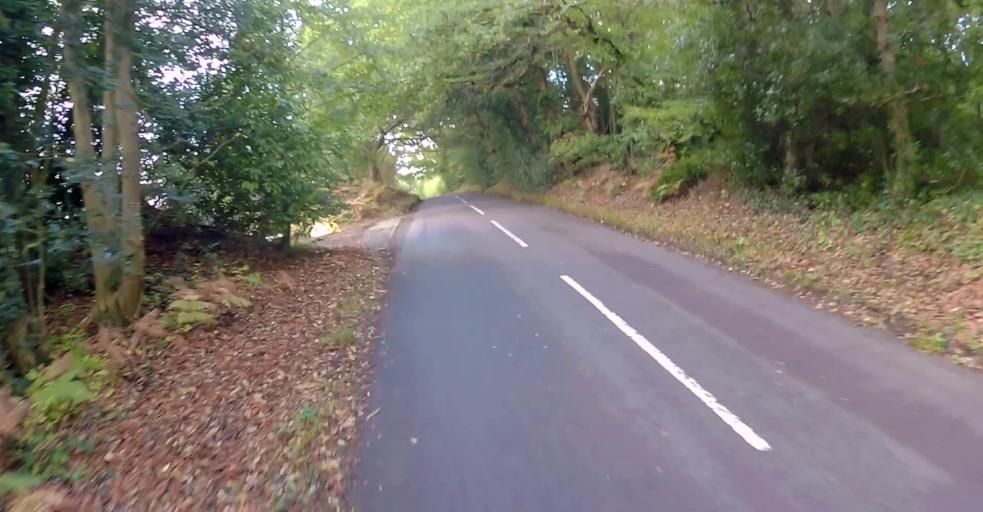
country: GB
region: England
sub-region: Surrey
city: Seale
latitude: 51.1938
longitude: -0.7411
